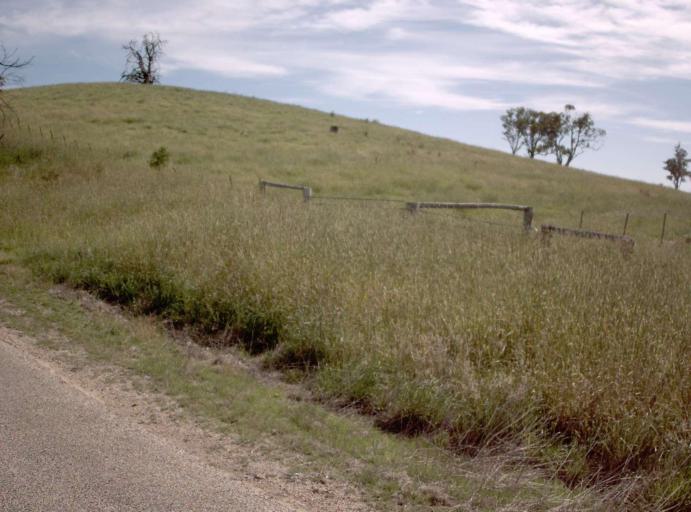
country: AU
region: Victoria
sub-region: East Gippsland
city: Lakes Entrance
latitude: -37.4994
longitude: 148.1327
